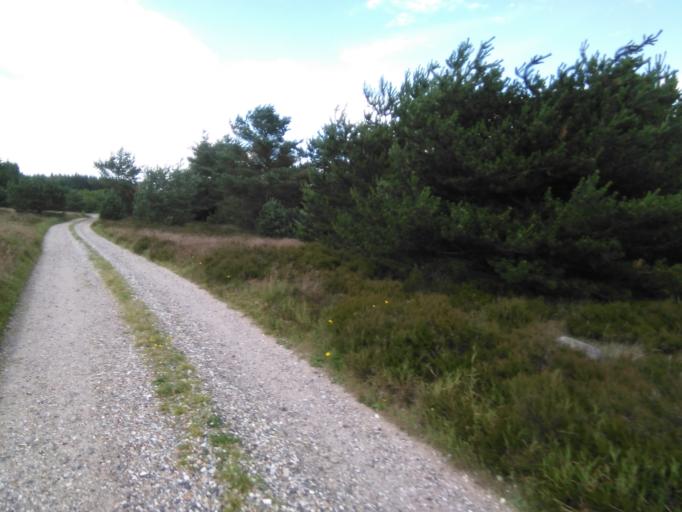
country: DK
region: Central Jutland
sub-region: Silkeborg Kommune
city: Virklund
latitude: 56.0879
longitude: 9.4321
